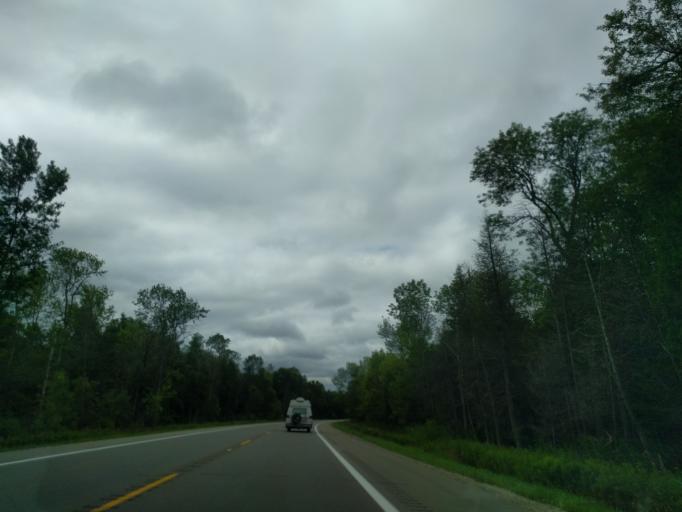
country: US
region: Michigan
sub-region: Menominee County
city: Menominee
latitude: 45.2841
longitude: -87.4536
